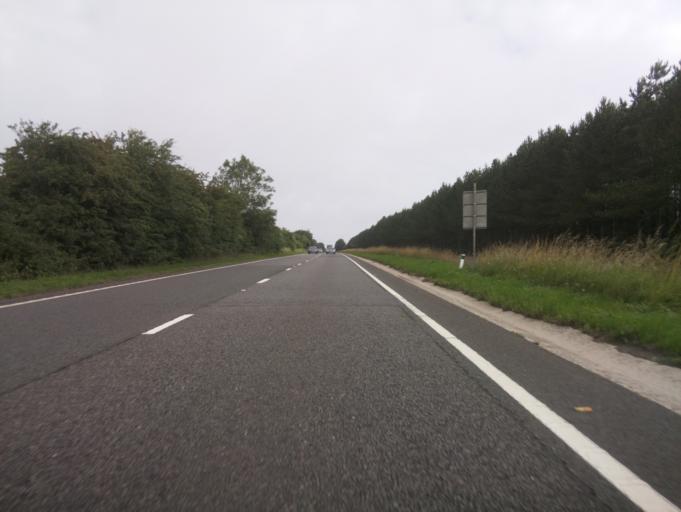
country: GB
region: England
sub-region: Gloucestershire
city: Coates
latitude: 51.7655
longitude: -2.0173
